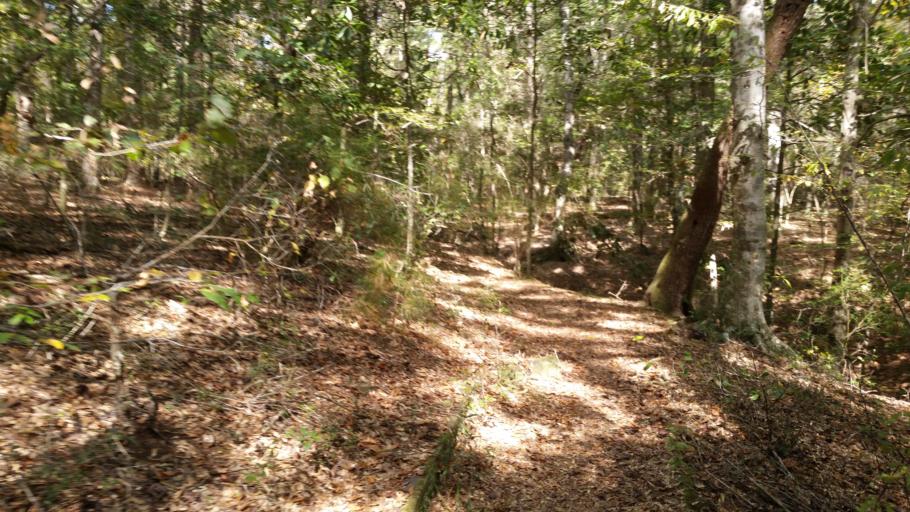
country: US
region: Alabama
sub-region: Baldwin County
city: Spanish Fort
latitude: 30.7408
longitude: -87.9237
